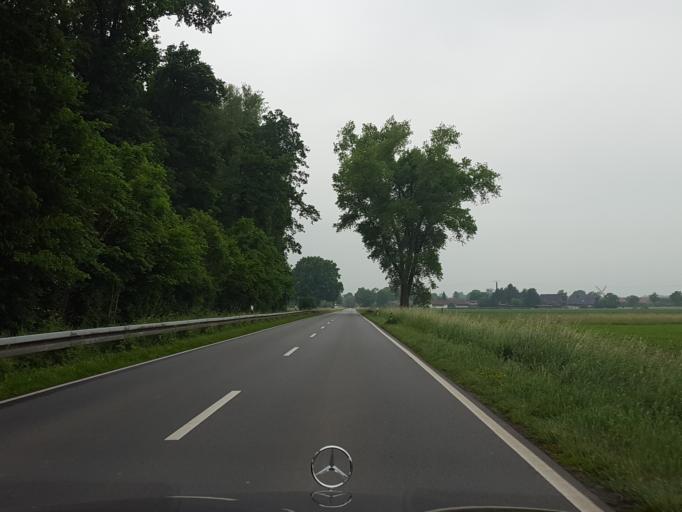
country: DE
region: North Rhine-Westphalia
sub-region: Regierungsbezirk Munster
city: Senden
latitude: 51.8247
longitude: 7.5618
